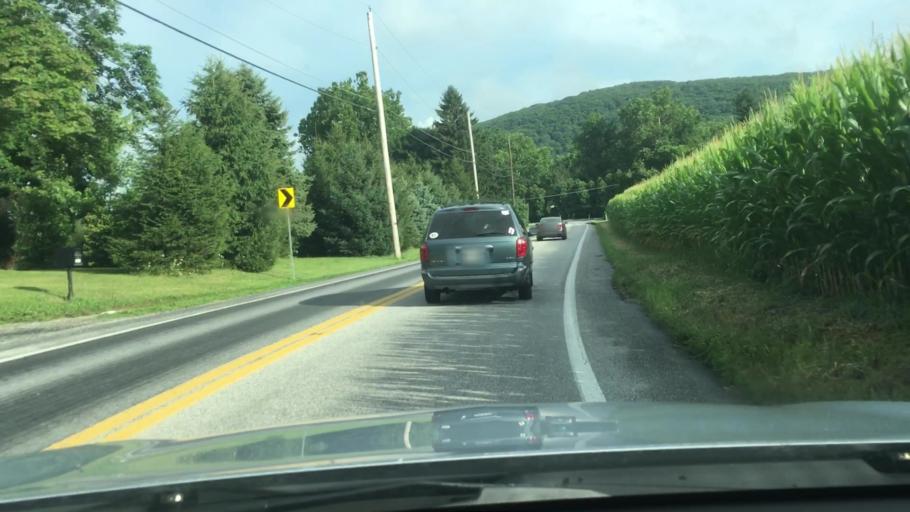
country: US
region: Pennsylvania
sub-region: York County
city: Dillsburg
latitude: 40.1472
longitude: -77.0647
